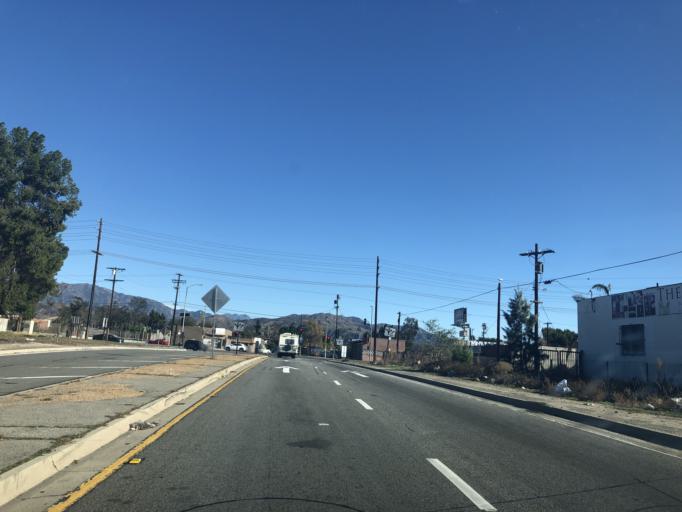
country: US
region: California
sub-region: Los Angeles County
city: North Hollywood
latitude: 34.2260
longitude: -118.3890
